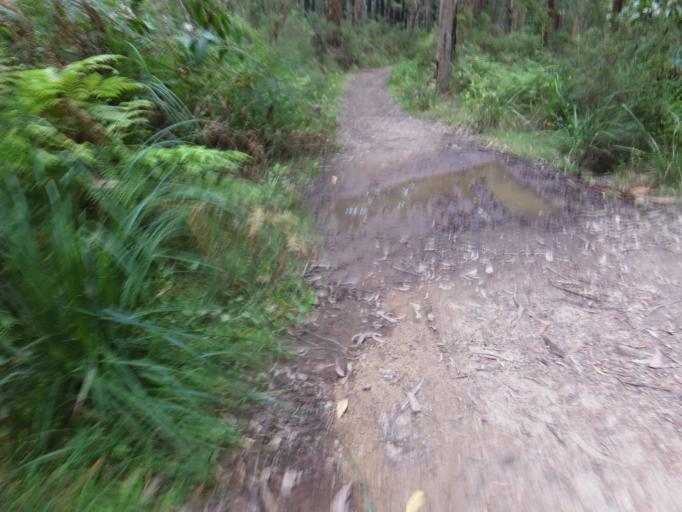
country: AU
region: Victoria
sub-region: Knox
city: The Basin
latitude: -37.8482
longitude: 145.3400
